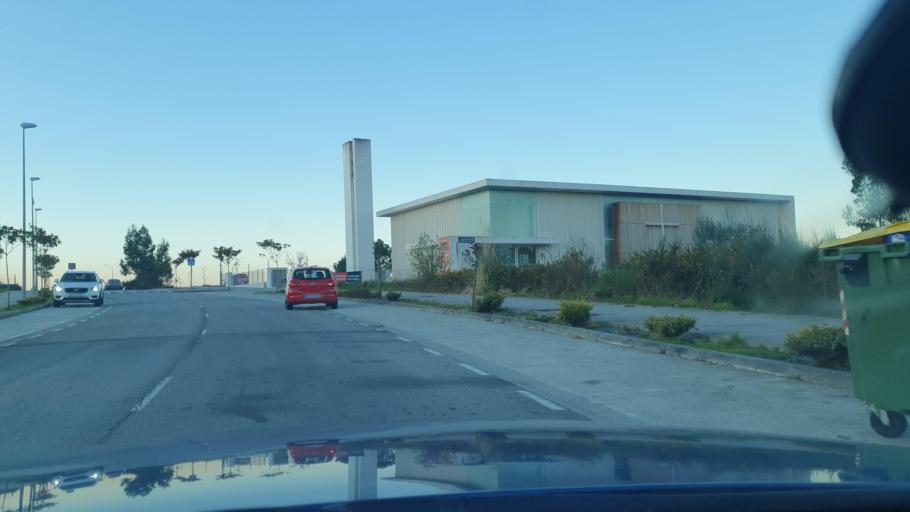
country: ES
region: Galicia
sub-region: Provincia da Coruna
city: Santiago de Compostela
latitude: 42.8474
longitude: -8.5827
